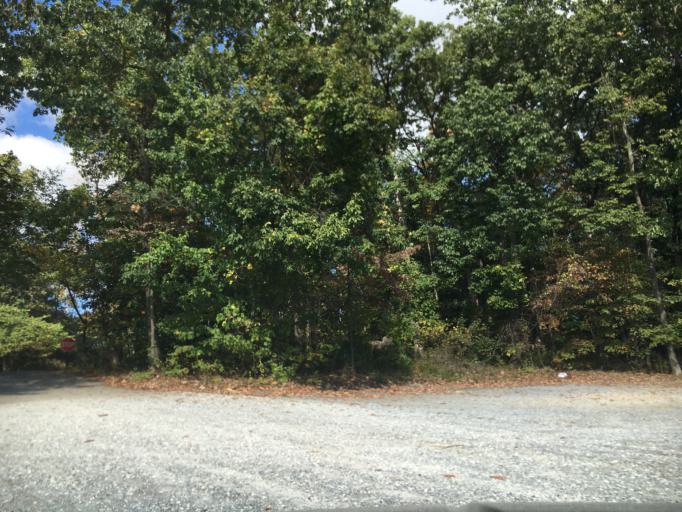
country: US
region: Pennsylvania
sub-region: York County
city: Yorklyn
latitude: 40.0083
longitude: -76.6624
